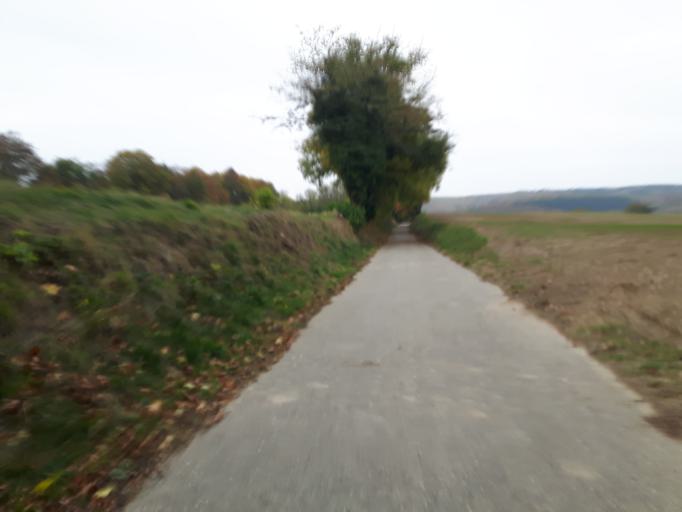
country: DE
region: Baden-Wuerttemberg
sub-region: Karlsruhe Region
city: Ostringen
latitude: 49.1931
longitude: 8.7309
